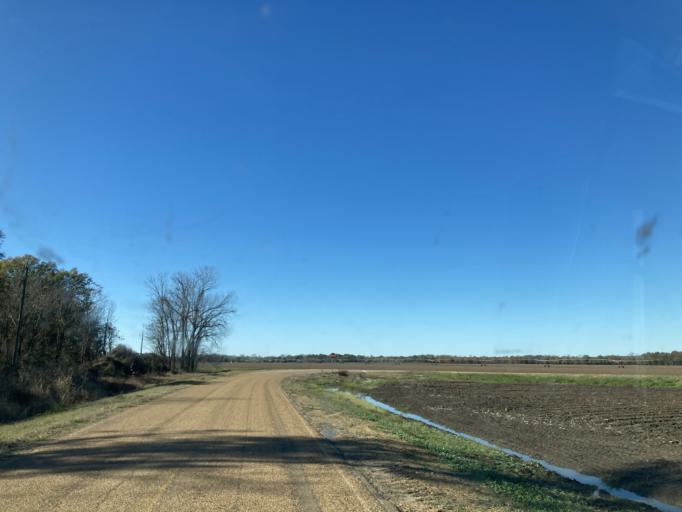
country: US
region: Mississippi
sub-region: Yazoo County
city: Yazoo City
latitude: 32.7396
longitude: -90.6355
